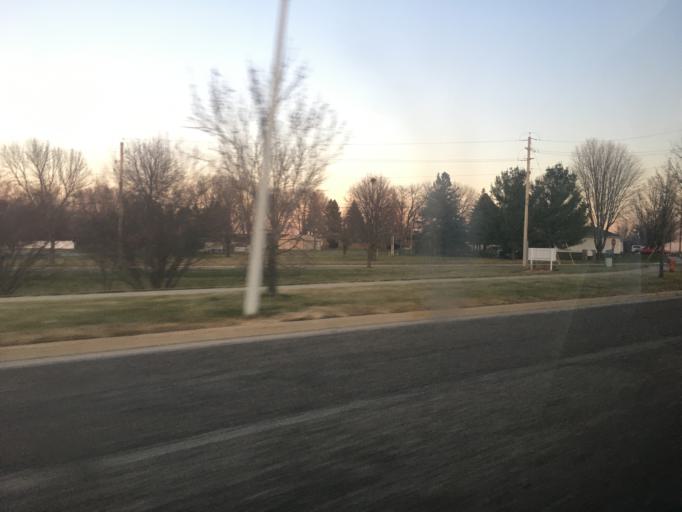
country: US
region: Minnesota
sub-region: Olmsted County
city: Rochester
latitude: 44.0726
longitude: -92.5102
